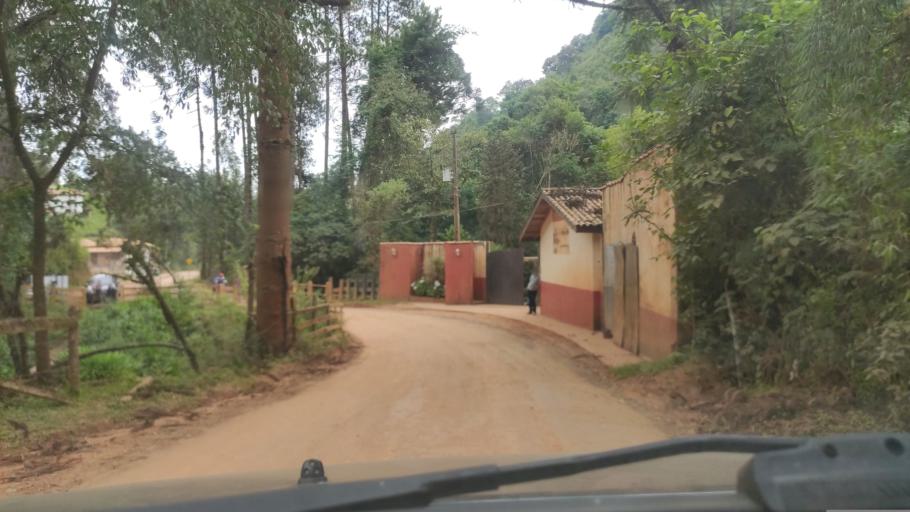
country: BR
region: Minas Gerais
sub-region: Paraisopolis
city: Paraisopolis
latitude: -22.6701
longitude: -45.8536
